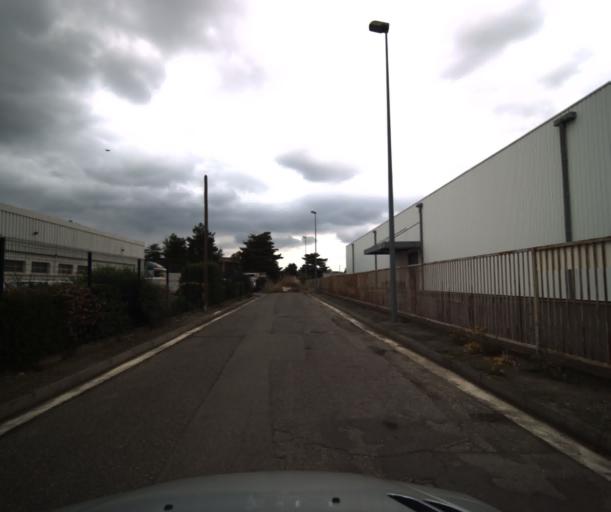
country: FR
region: Midi-Pyrenees
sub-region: Departement de la Haute-Garonne
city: Pinsaguel
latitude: 43.5326
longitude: 1.3841
